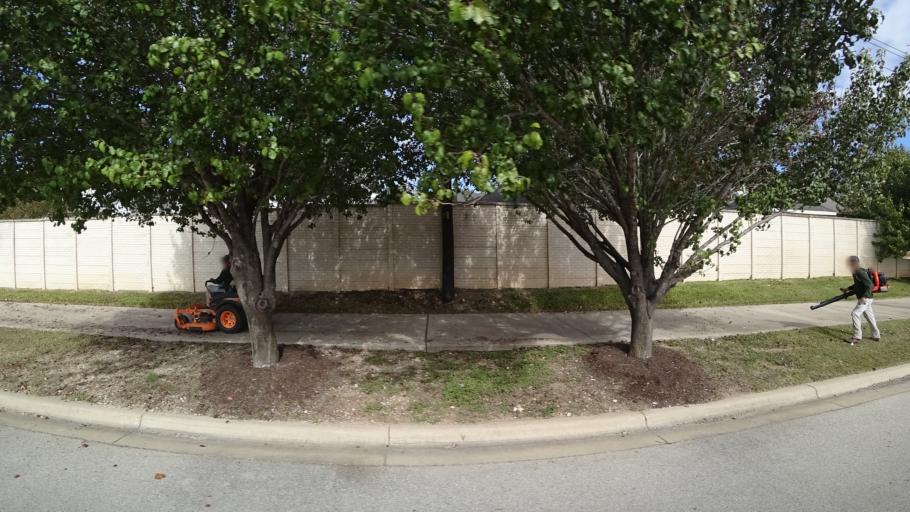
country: US
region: Texas
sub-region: Travis County
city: Pflugerville
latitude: 30.4376
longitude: -97.6423
